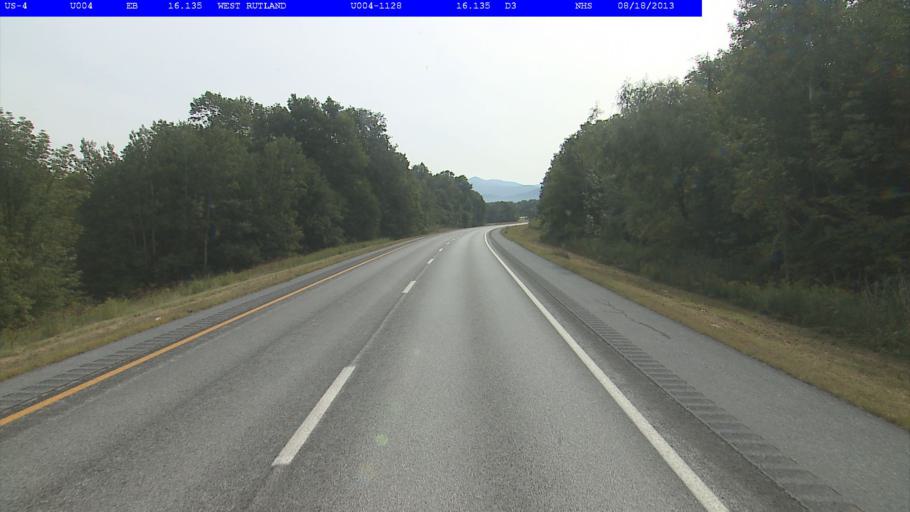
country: US
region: Vermont
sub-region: Rutland County
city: West Rutland
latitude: 43.5927
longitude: -73.0160
